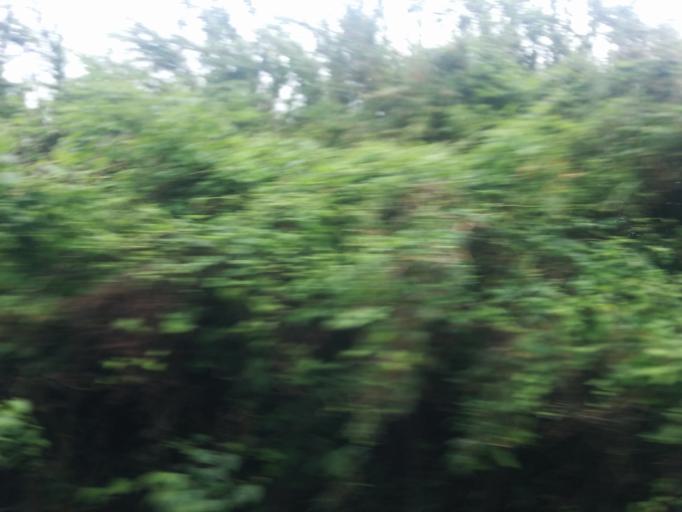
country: JP
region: Tochigi
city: Imaichi
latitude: 36.6751
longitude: 139.7272
